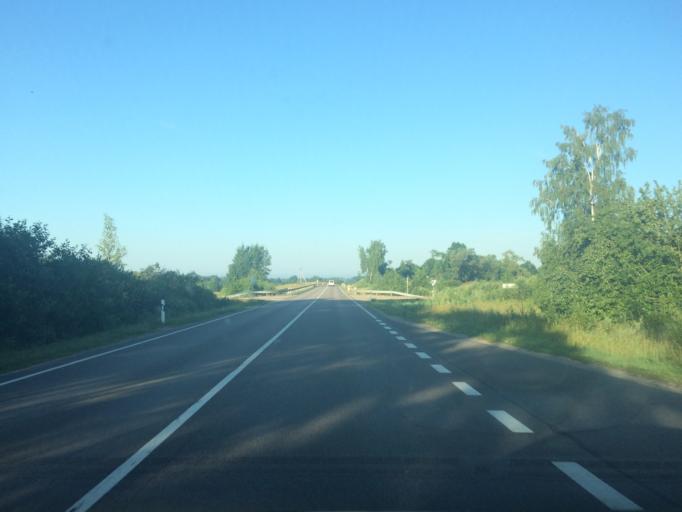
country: LT
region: Utenos apskritis
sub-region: Anyksciai
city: Anyksciai
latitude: 55.4220
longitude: 25.2239
